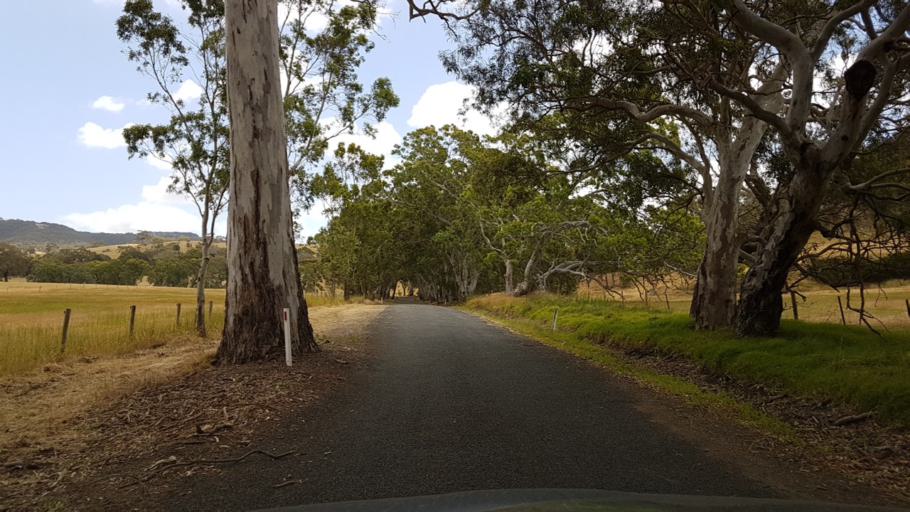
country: AU
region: South Australia
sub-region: Victor Harbor
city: Victor Harbor
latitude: -35.4687
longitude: 138.5968
